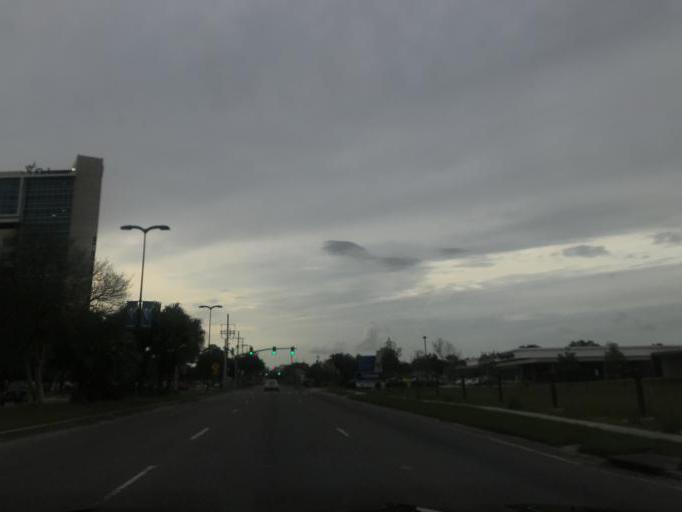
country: US
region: Louisiana
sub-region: Jefferson Parish
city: Jefferson
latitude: 29.9628
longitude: -90.1446
